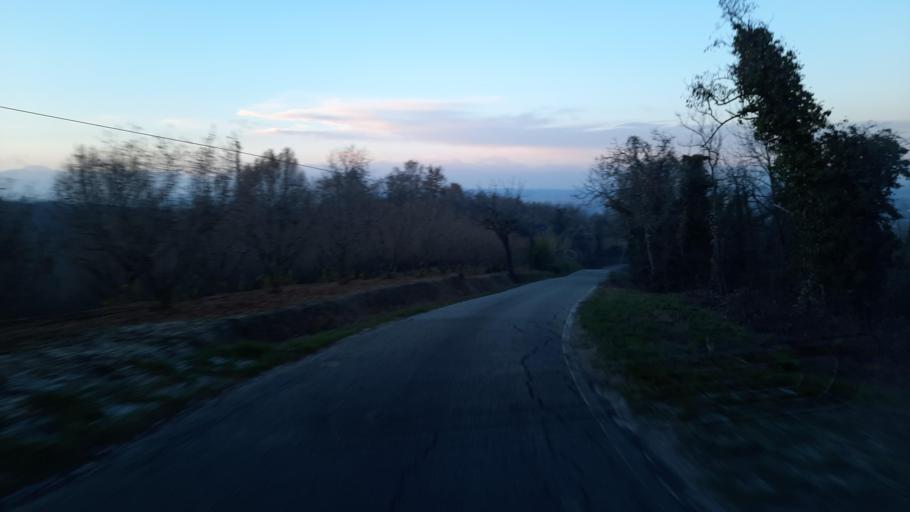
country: IT
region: Piedmont
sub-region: Provincia di Alessandria
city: Camino
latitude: 45.1713
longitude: 8.2770
